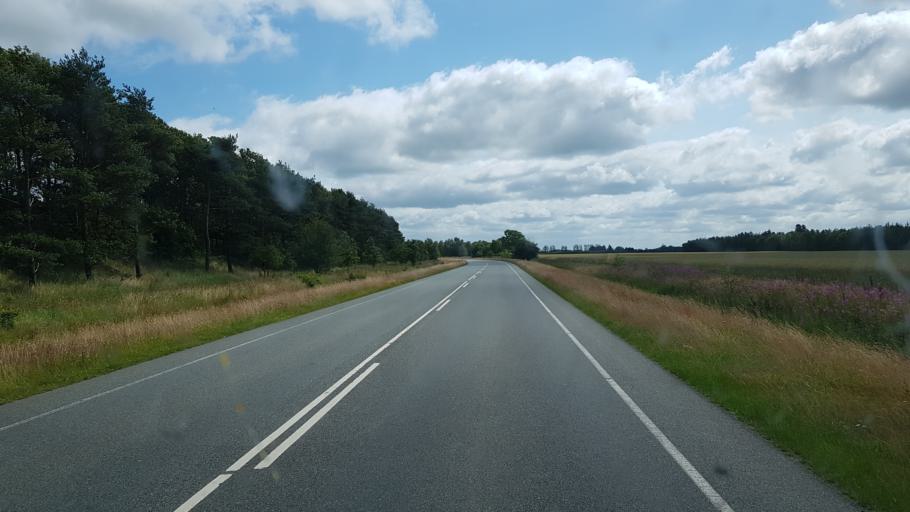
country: DK
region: South Denmark
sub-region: Billund Kommune
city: Grindsted
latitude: 55.7524
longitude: 8.9026
